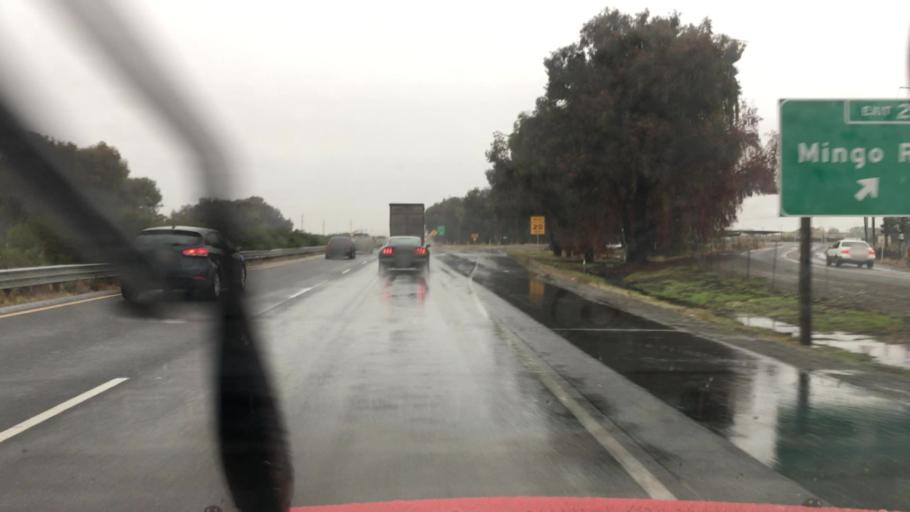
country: US
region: California
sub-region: Sacramento County
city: Galt
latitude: 38.3008
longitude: -121.3171
